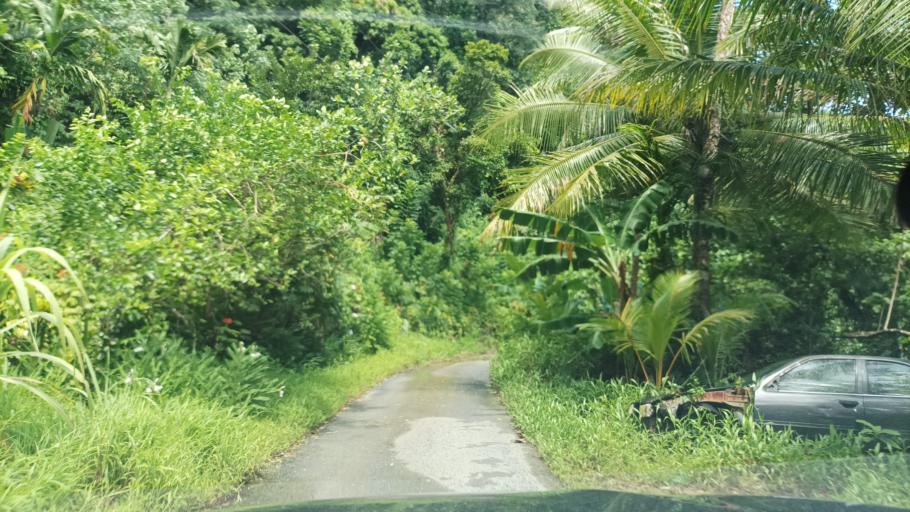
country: FM
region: Pohnpei
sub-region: Sokehs Municipality
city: Palikir - National Government Center
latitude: 6.9430
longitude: 158.1628
